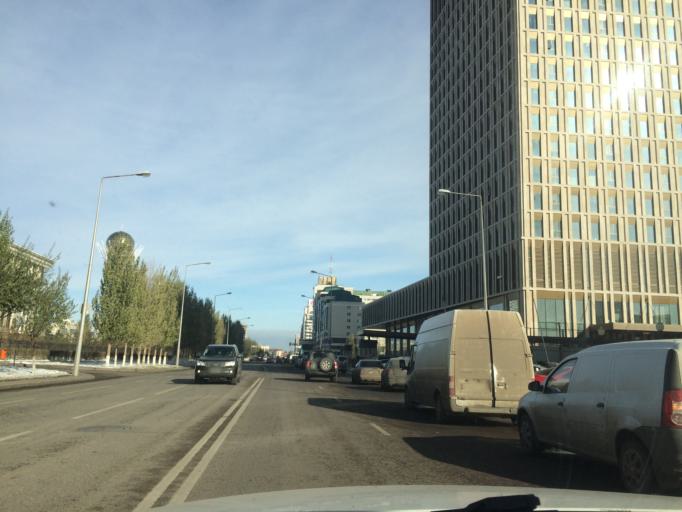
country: KZ
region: Astana Qalasy
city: Astana
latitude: 51.1236
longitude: 71.4306
